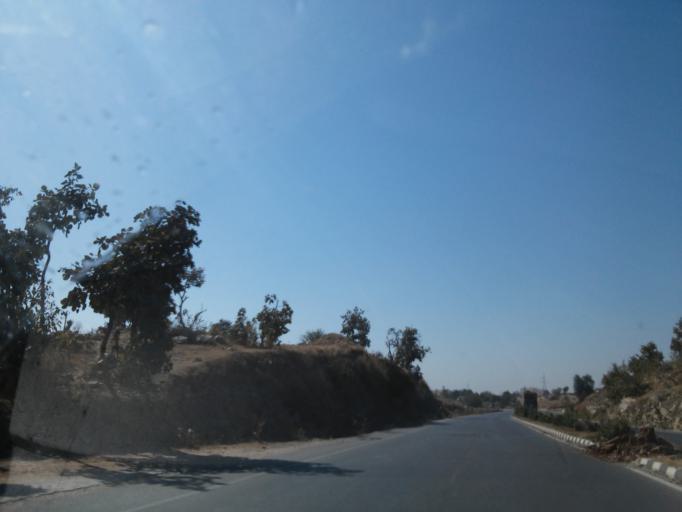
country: IN
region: Rajasthan
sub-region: Dungarpur
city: Dungarpur
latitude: 23.9493
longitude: 73.5770
